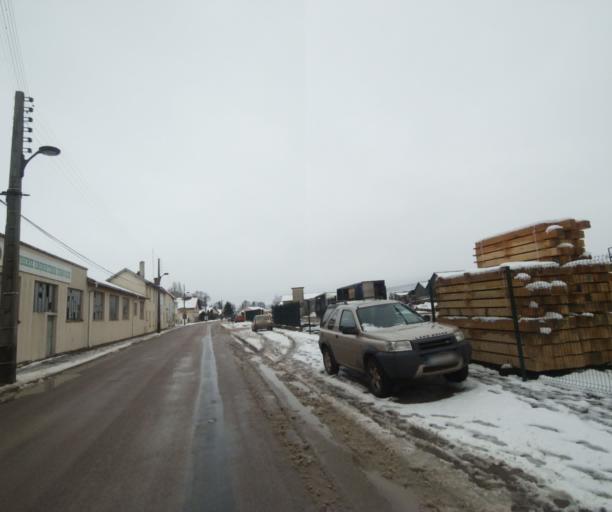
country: FR
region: Champagne-Ardenne
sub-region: Departement de la Haute-Marne
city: Montier-en-Der
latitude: 48.4750
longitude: 4.7729
